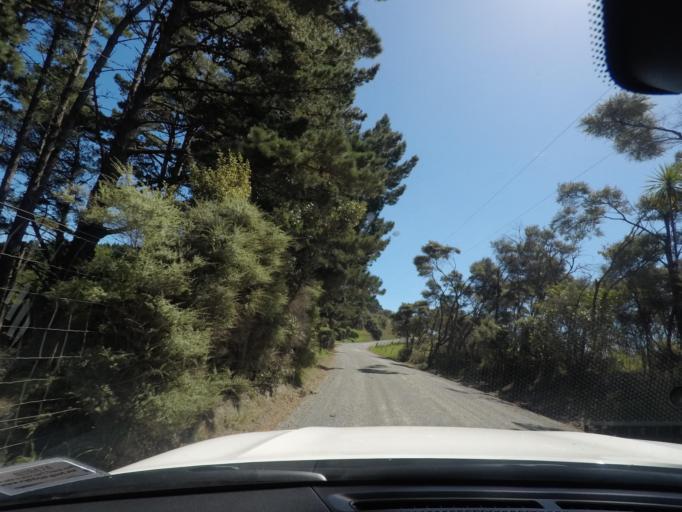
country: NZ
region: Auckland
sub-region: Auckland
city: Parakai
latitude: -36.5825
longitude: 174.3014
